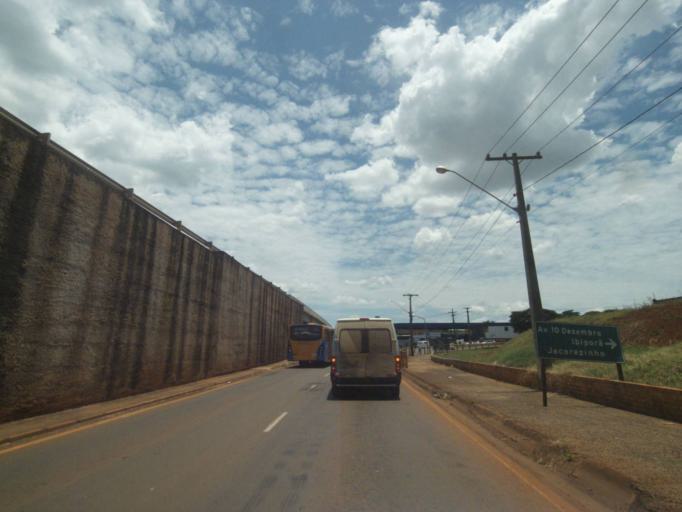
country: BR
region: Parana
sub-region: Londrina
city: Londrina
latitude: -23.3606
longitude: -51.1507
